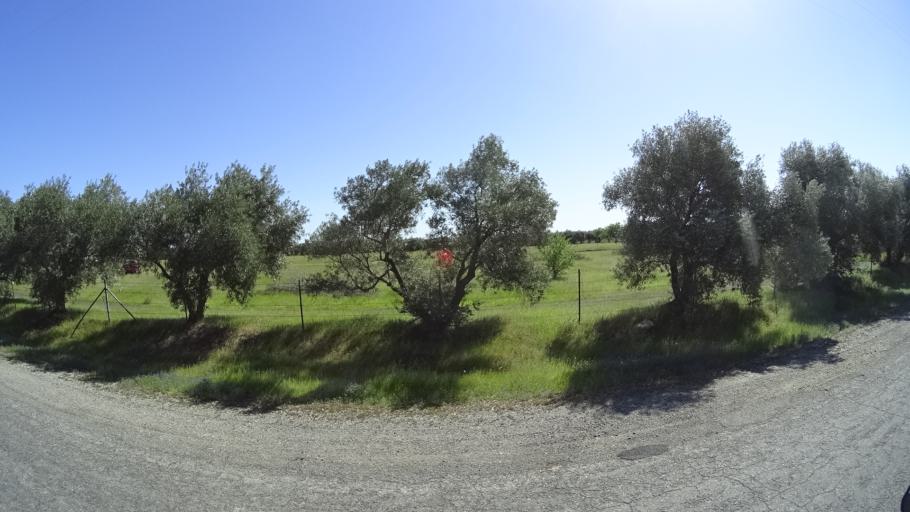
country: US
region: California
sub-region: Glenn County
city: Orland
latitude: 39.7239
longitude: -122.2112
